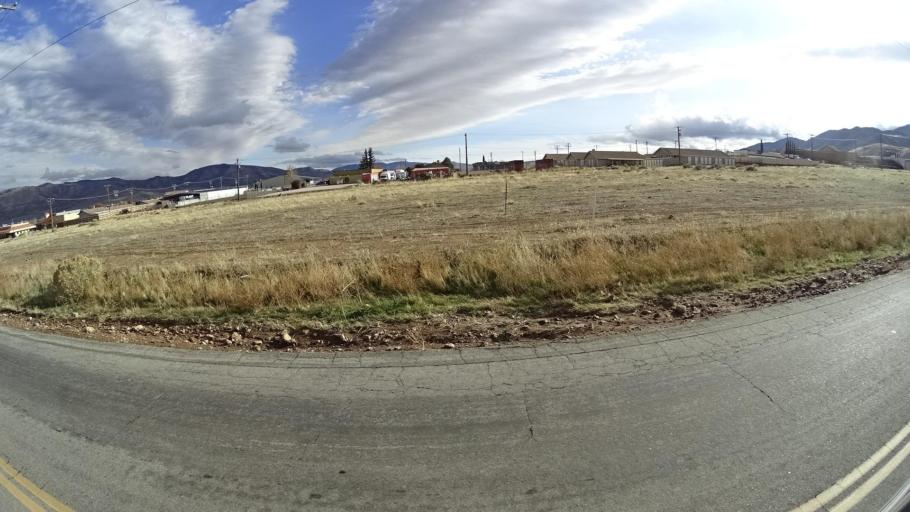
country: US
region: California
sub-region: Kern County
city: Golden Hills
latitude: 35.1219
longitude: -118.4951
